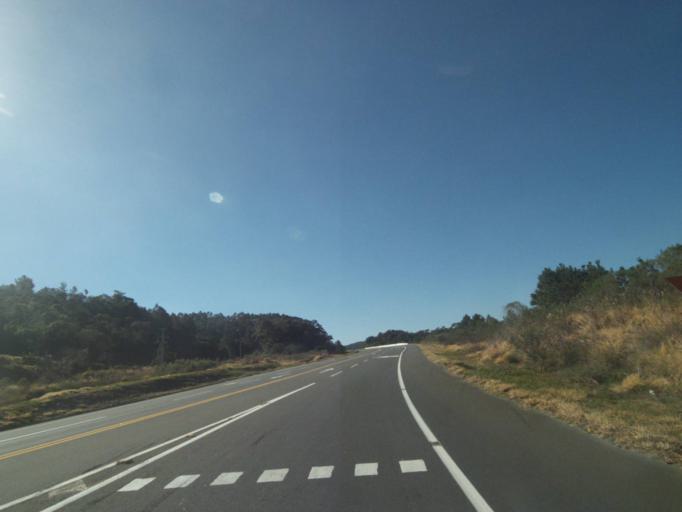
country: BR
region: Parana
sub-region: Tibagi
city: Tibagi
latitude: -24.8140
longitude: -50.4852
